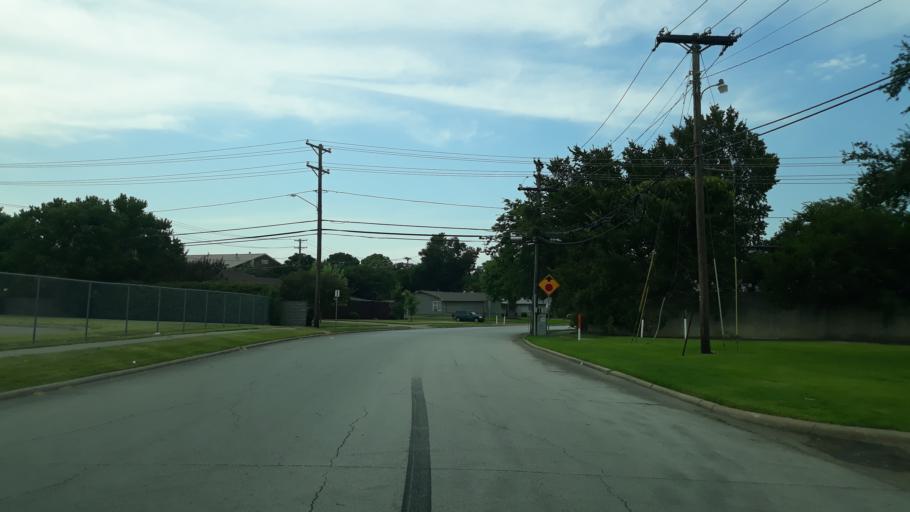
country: US
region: Texas
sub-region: Dallas County
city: Irving
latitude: 32.8388
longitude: -96.9857
